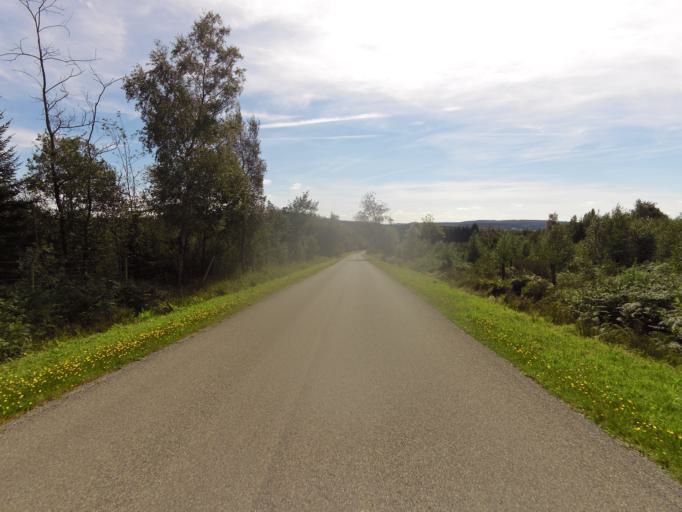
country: BE
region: Wallonia
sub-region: Province du Luxembourg
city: Saint-Hubert
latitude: 50.0453
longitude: 5.3529
